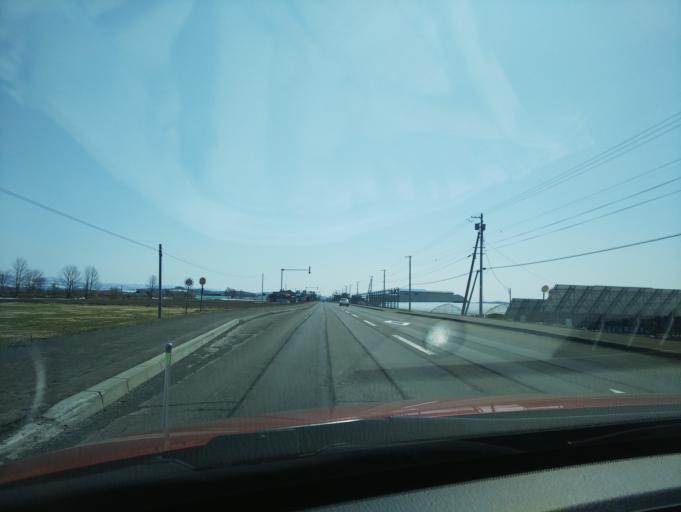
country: JP
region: Hokkaido
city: Nayoro
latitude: 44.2155
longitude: 142.3949
